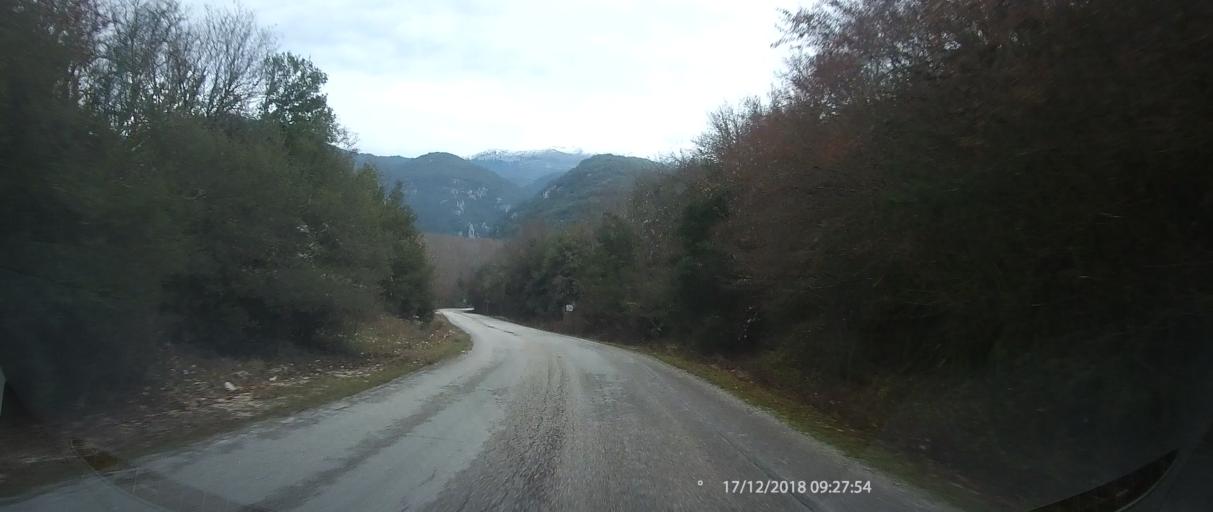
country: GR
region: Epirus
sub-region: Nomos Ioanninon
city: Kalpaki
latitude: 39.9446
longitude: 20.6831
